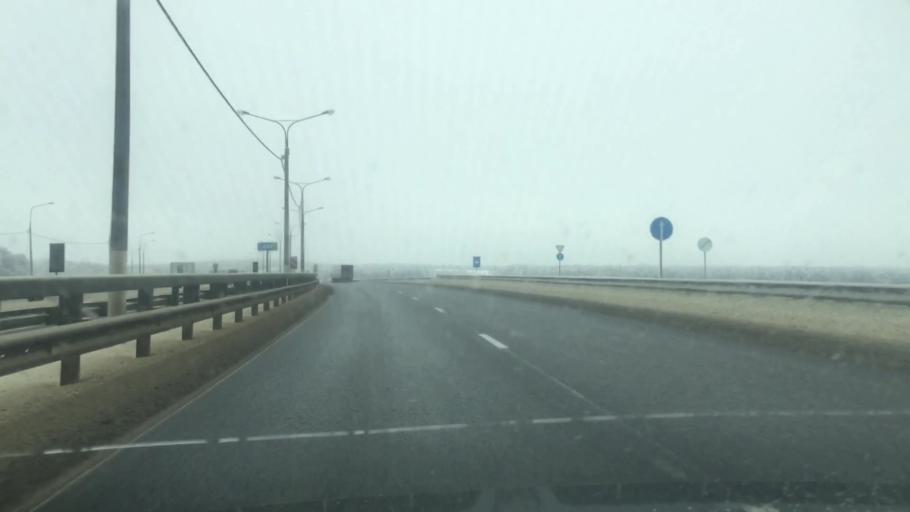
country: RU
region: Lipetsk
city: Yelets
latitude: 52.5429
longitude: 38.7222
